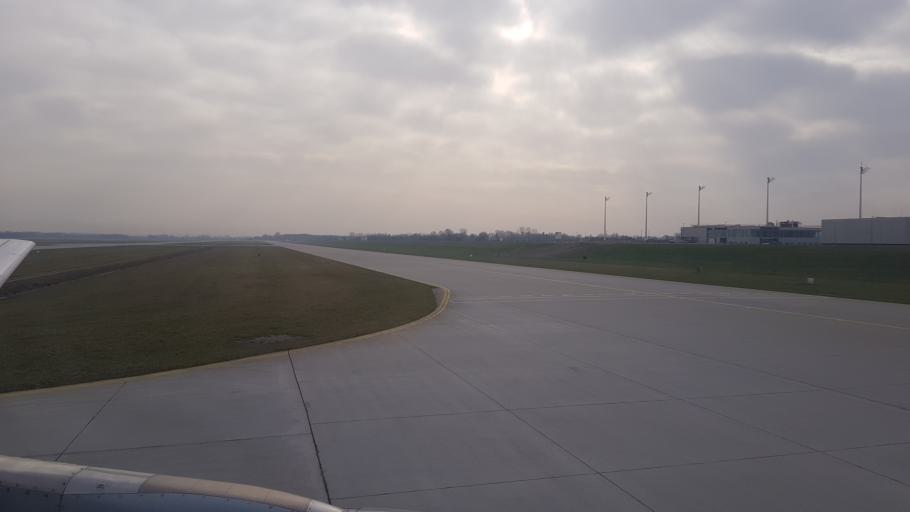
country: DE
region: Bavaria
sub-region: Upper Bavaria
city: Marzling
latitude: 48.3616
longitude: 11.7986
